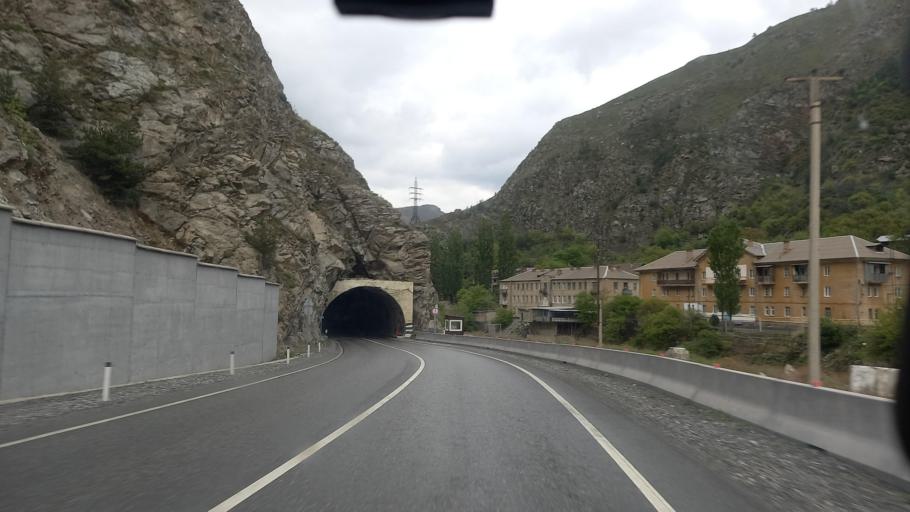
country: RU
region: North Ossetia
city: Mizur
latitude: 42.8477
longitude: 44.0500
